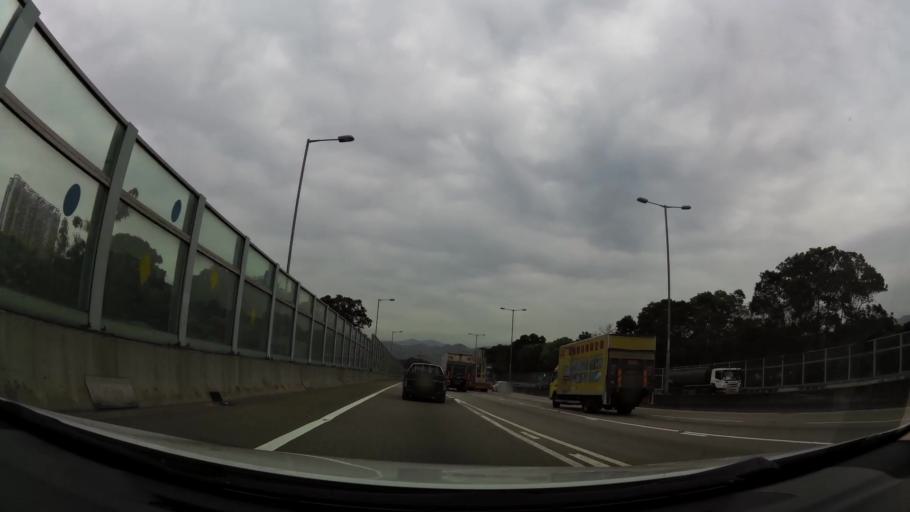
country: HK
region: Yuen Long
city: Yuen Long Kau Hui
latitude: 22.4373
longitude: 114.0167
